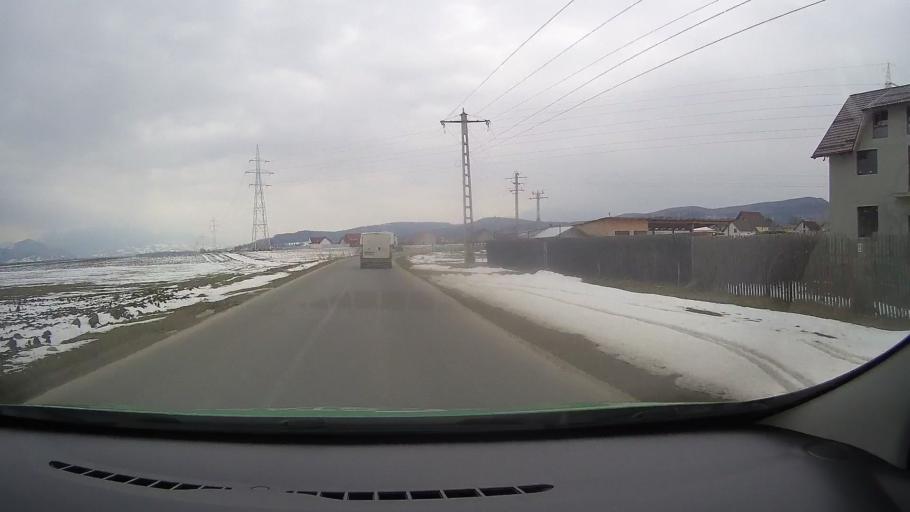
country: RO
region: Brasov
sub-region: Comuna Vulcan
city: Vulcan
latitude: 45.6357
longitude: 25.4297
